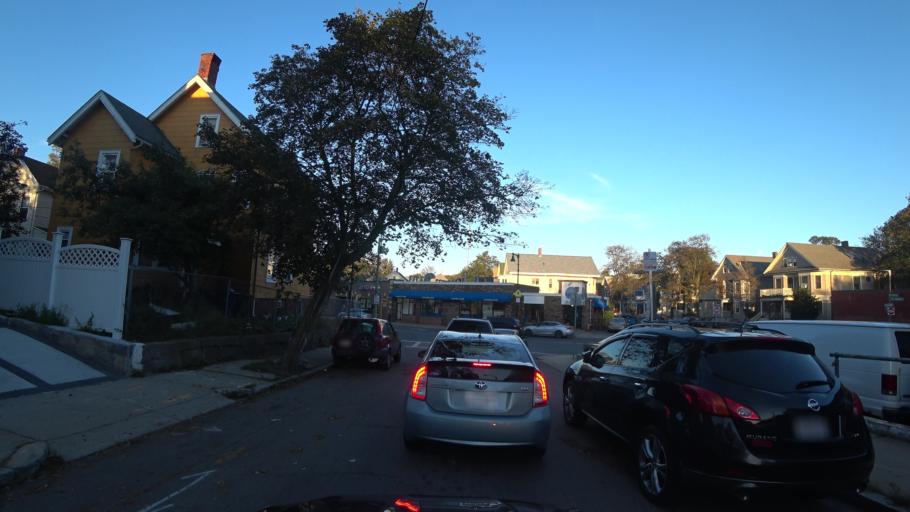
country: US
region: Massachusetts
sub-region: Suffolk County
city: South Boston
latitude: 42.2928
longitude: -71.0629
